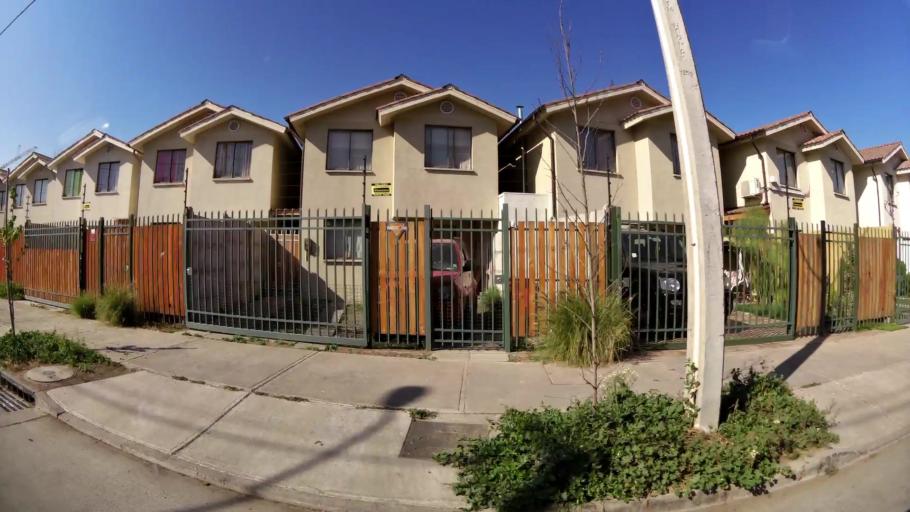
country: CL
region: Santiago Metropolitan
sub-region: Provincia de Chacabuco
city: Chicureo Abajo
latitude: -33.3540
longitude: -70.6850
